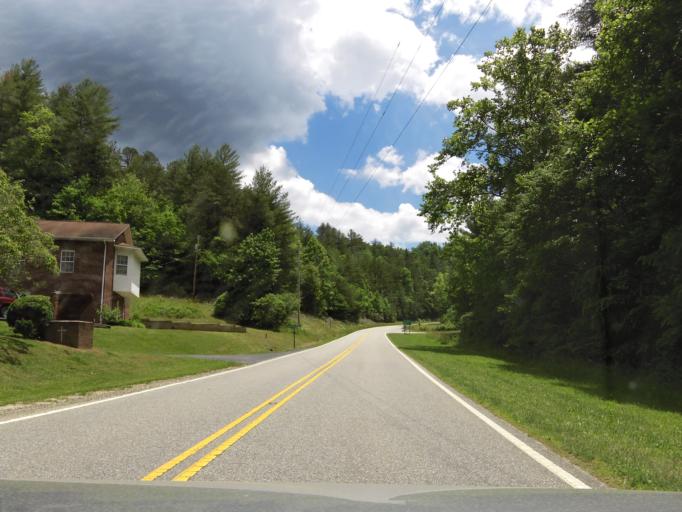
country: US
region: North Carolina
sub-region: Graham County
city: Robbinsville
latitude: 35.3895
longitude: -83.8642
